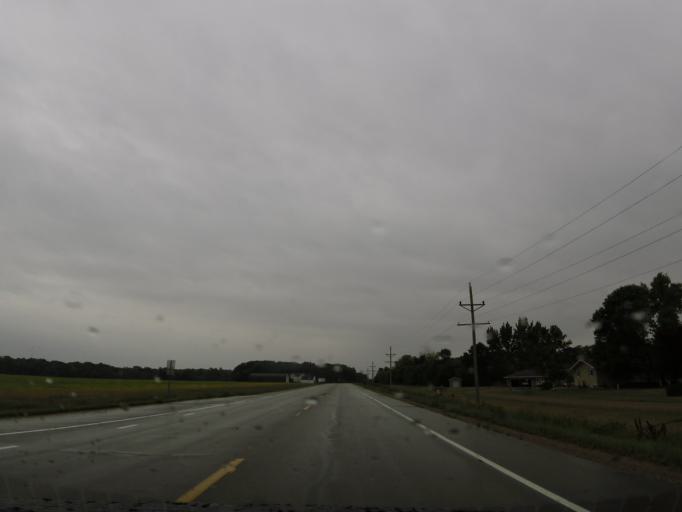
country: US
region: Minnesota
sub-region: Marshall County
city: Warren
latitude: 48.4481
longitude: -96.8673
